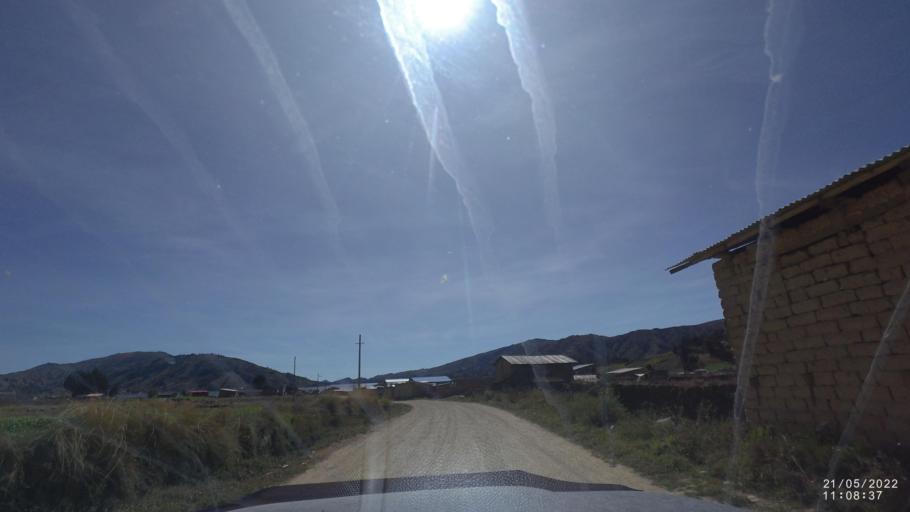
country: BO
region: Cochabamba
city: Colomi
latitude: -17.3056
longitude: -65.9113
